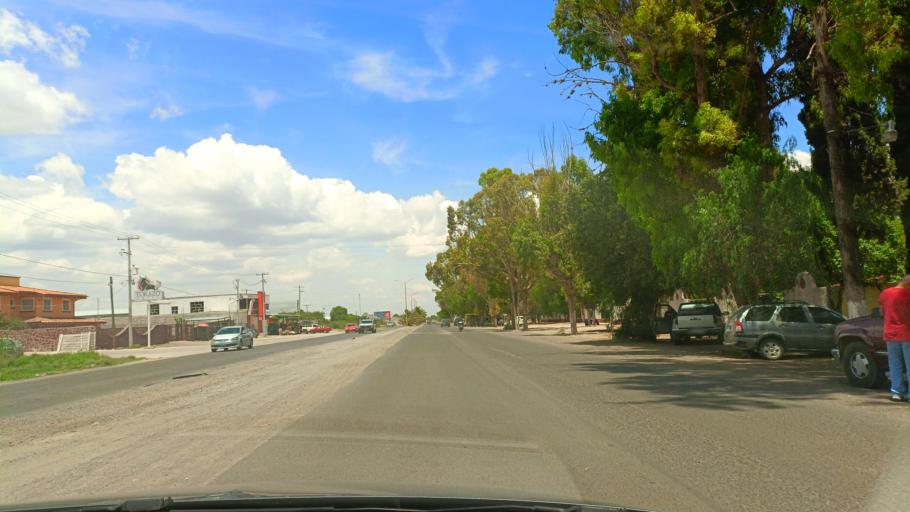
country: MX
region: Guanajuato
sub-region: San Luis de la Paz
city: San Ignacio
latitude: 21.2903
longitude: -100.5479
